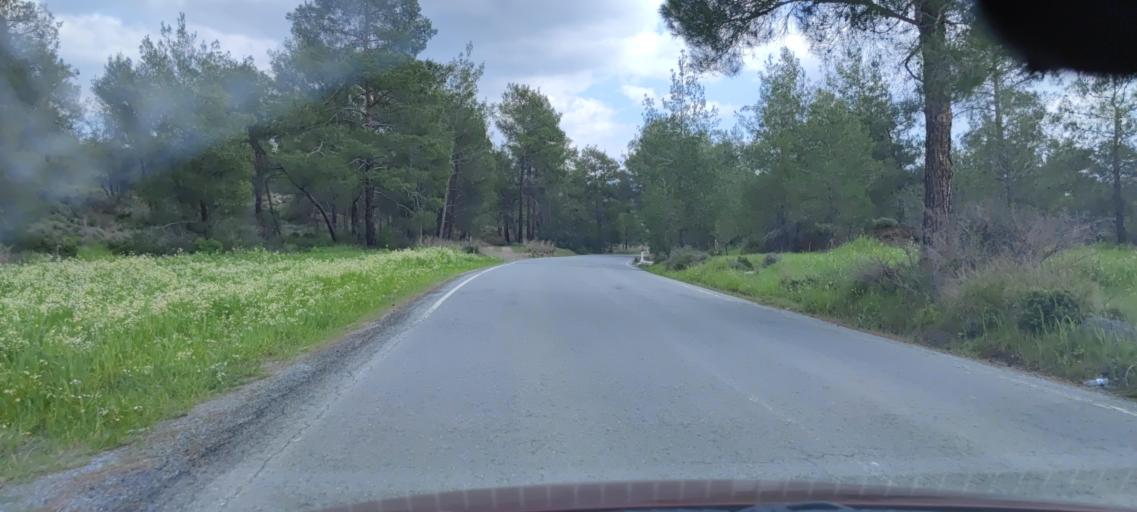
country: CY
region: Larnaka
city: Kornos
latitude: 34.9181
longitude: 33.3561
